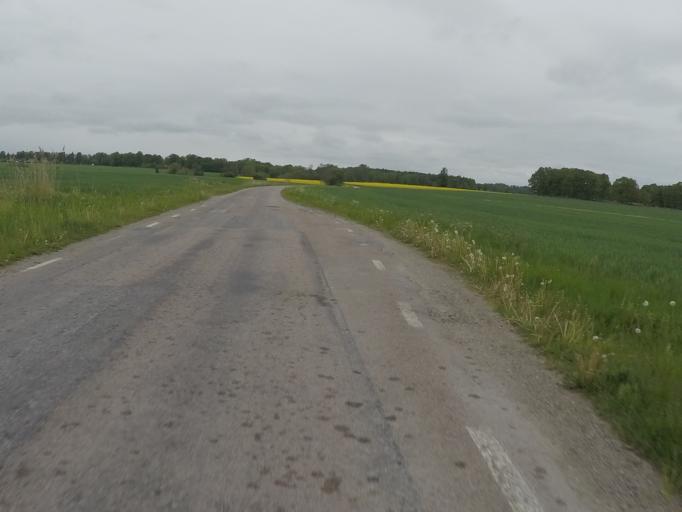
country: SE
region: Vaestmanland
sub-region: Hallstahammars Kommun
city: Kolback
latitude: 59.5505
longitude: 16.2781
